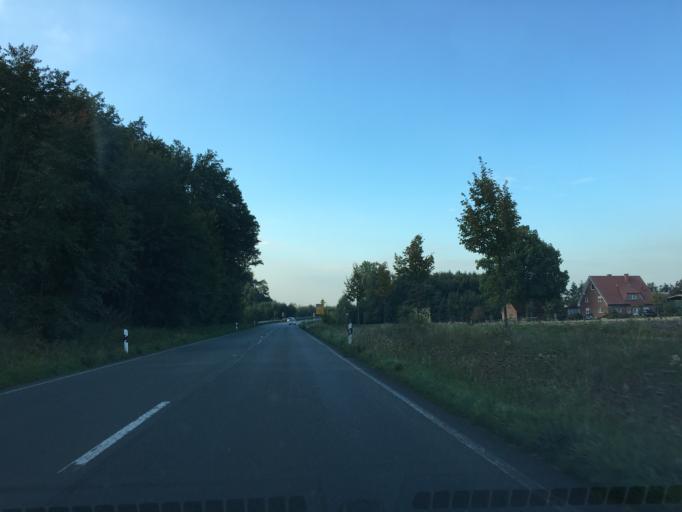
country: DE
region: North Rhine-Westphalia
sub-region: Regierungsbezirk Munster
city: Dulmen
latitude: 51.7955
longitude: 7.3388
